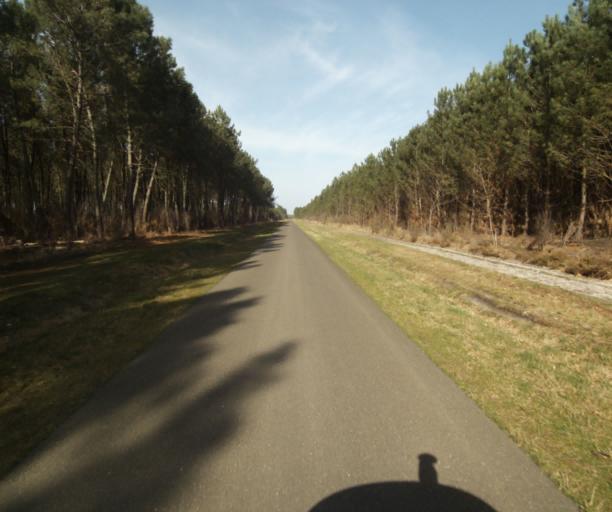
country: FR
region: Aquitaine
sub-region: Departement des Landes
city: Roquefort
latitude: 44.2040
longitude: -0.1992
